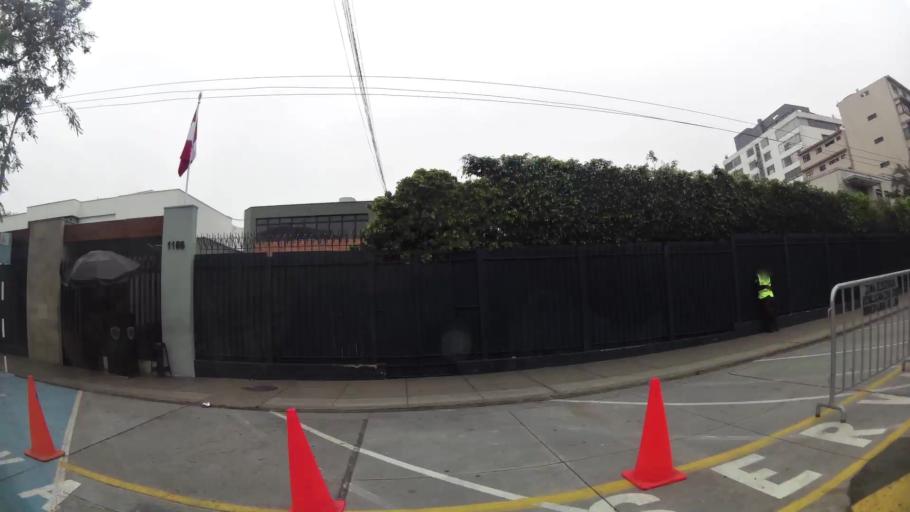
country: PE
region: Lima
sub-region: Lima
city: San Isidro
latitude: -12.1148
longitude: -77.0405
